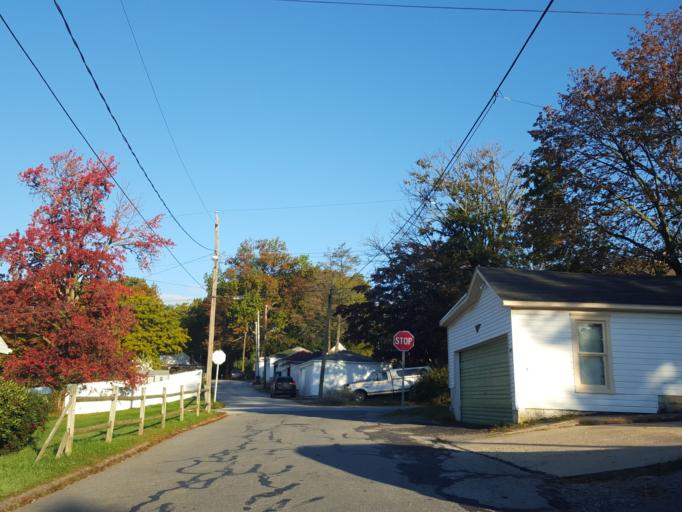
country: US
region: Pennsylvania
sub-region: York County
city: Red Lion
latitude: 39.9057
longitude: -76.6115
